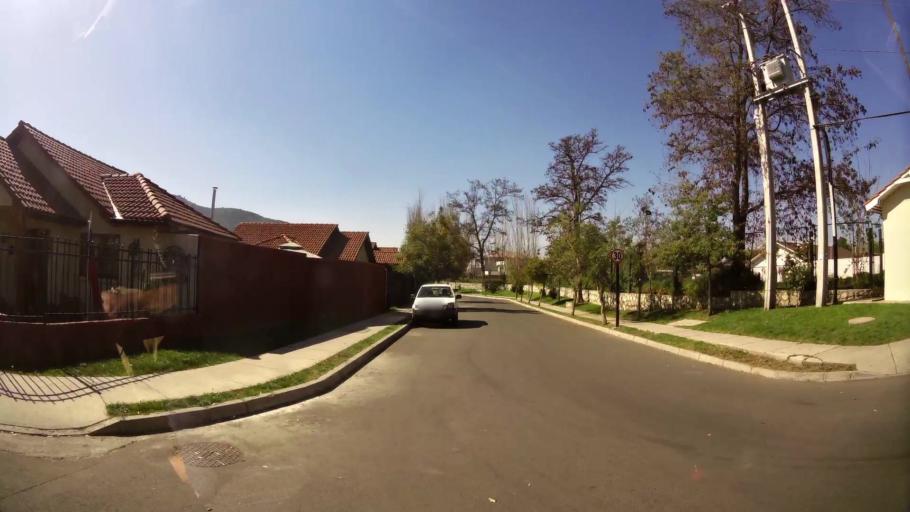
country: CL
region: Santiago Metropolitan
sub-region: Provincia de Talagante
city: Penaflor
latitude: -33.6066
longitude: -70.9050
